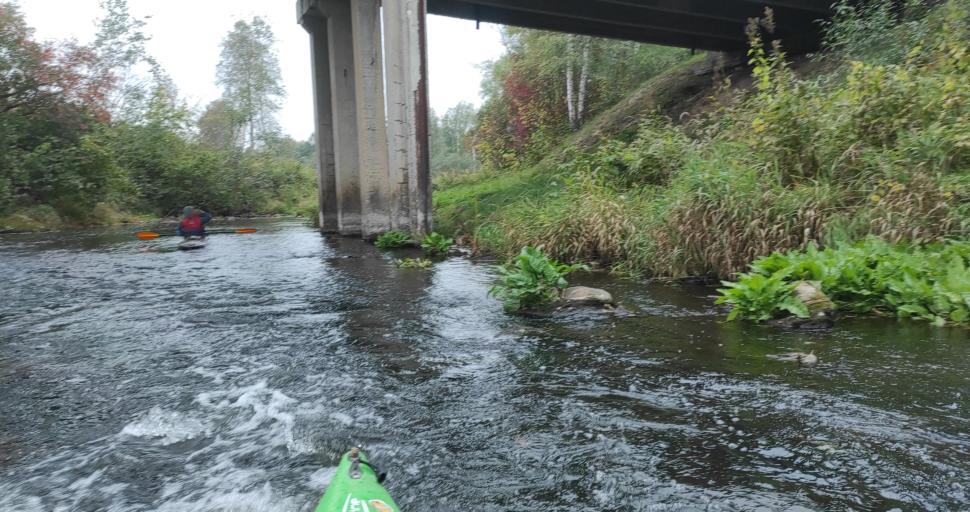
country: LV
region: Skrunda
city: Skrunda
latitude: 56.7059
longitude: 22.2094
